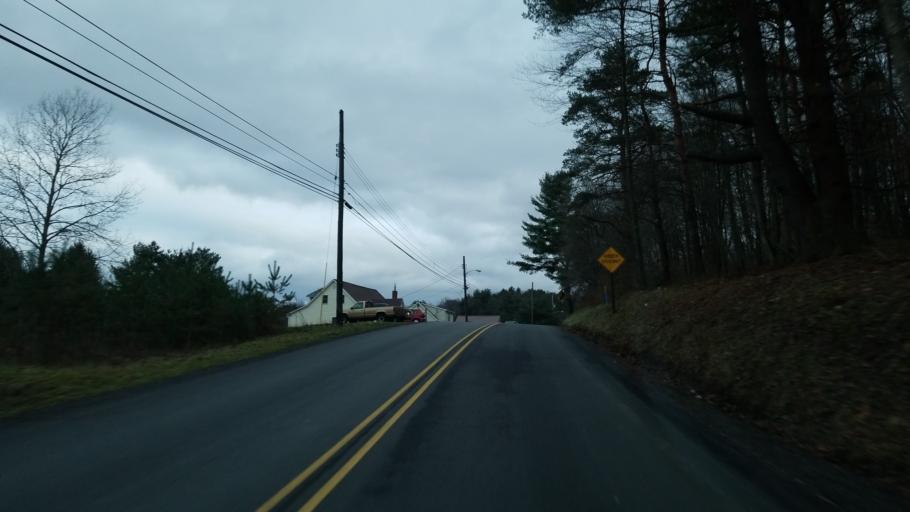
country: US
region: Pennsylvania
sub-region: Clearfield County
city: Sandy
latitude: 41.1173
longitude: -78.7936
